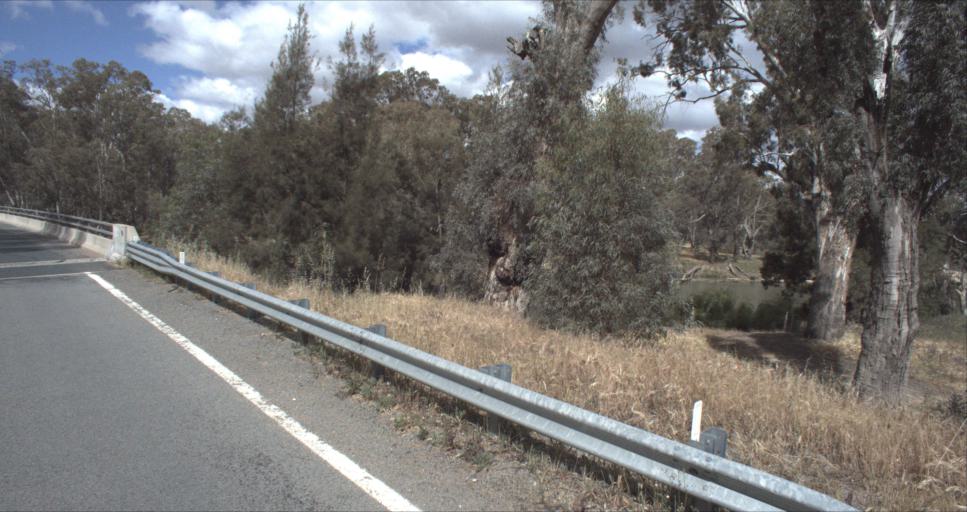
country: AU
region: New South Wales
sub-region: Leeton
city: Leeton
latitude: -34.6392
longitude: 146.3732
